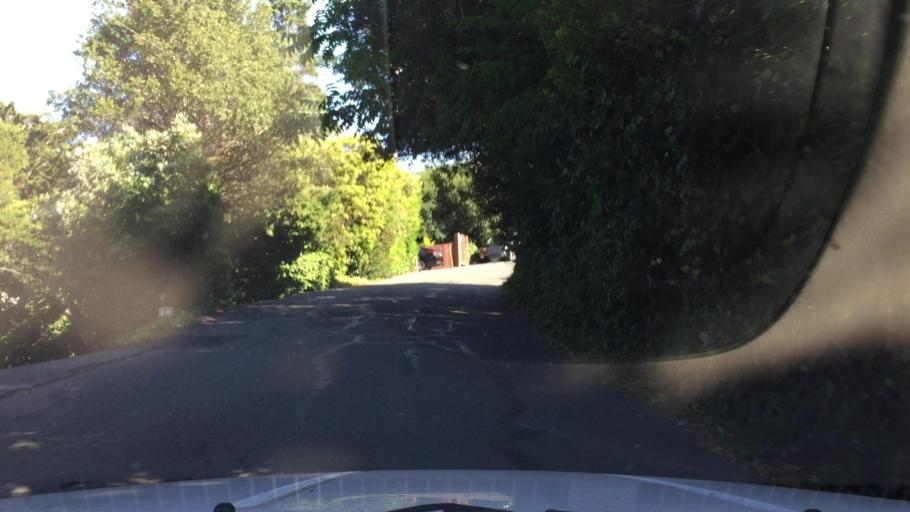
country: US
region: California
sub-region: Marin County
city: Sausalito
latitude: 37.8566
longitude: -122.4913
